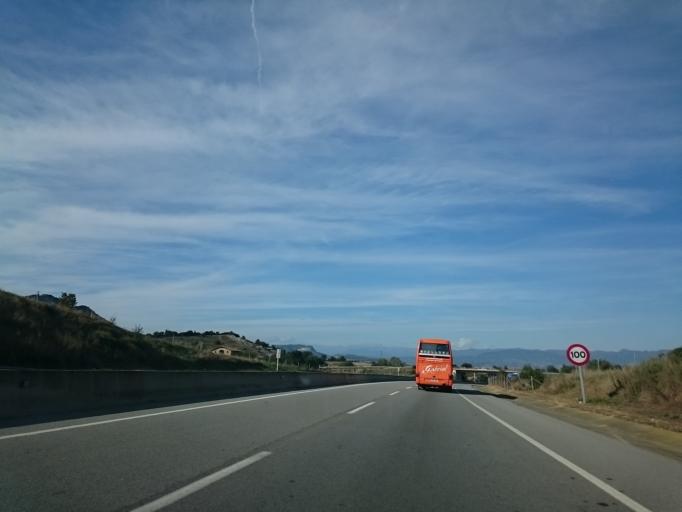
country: ES
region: Catalonia
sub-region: Provincia de Barcelona
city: Gurb
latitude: 41.9313
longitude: 2.2302
